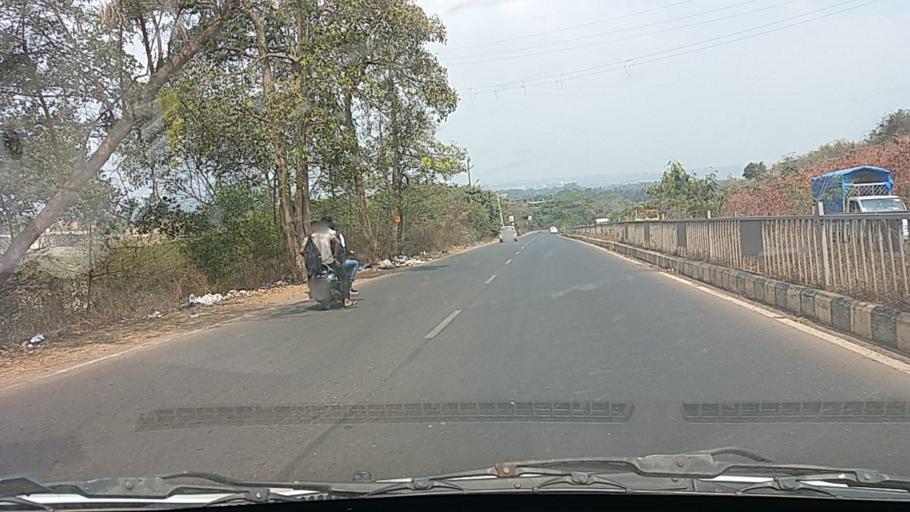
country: IN
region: Goa
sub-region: North Goa
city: Bambolim
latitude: 15.4655
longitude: 73.8521
